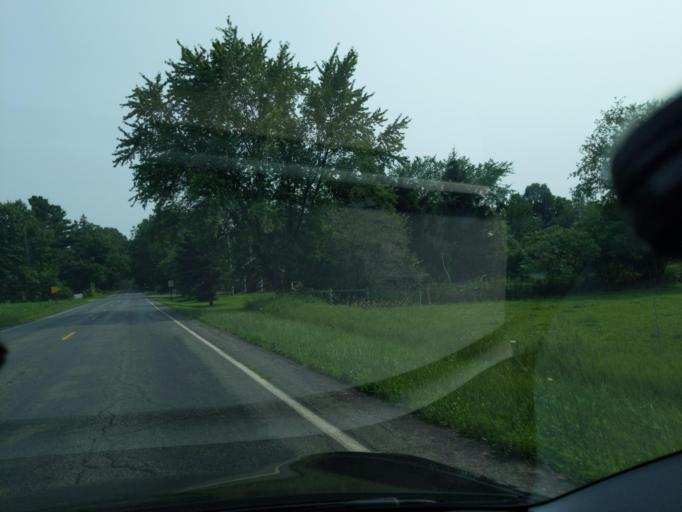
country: US
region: Michigan
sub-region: Eaton County
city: Eaton Rapids
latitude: 42.4959
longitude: -84.5610
